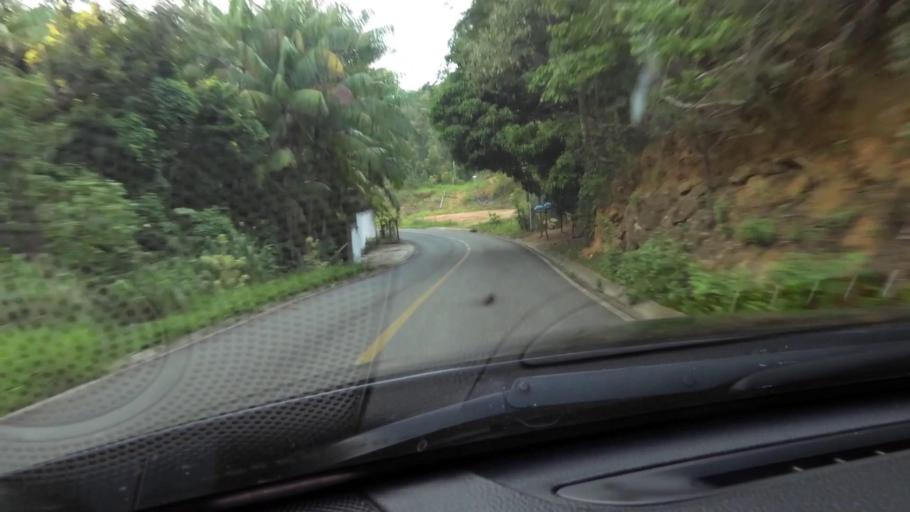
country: BR
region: Espirito Santo
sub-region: Guarapari
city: Guarapari
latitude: -20.5961
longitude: -40.5390
